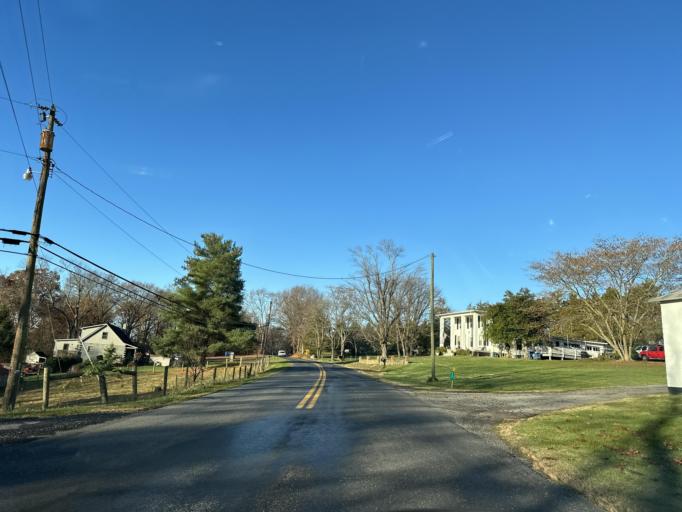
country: US
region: Virginia
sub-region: Augusta County
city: Weyers Cave
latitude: 38.2969
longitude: -78.9450
